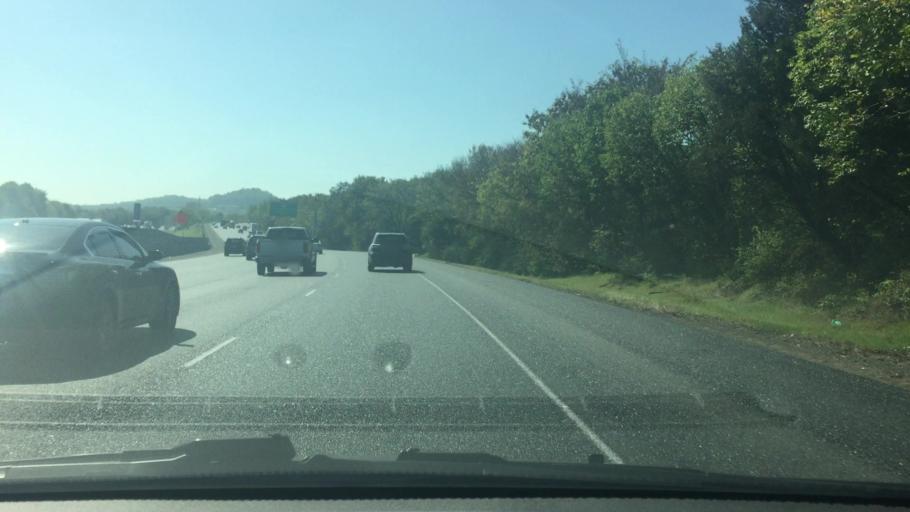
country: US
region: Tennessee
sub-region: Williamson County
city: Brentwood
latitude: 36.0549
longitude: -86.7753
